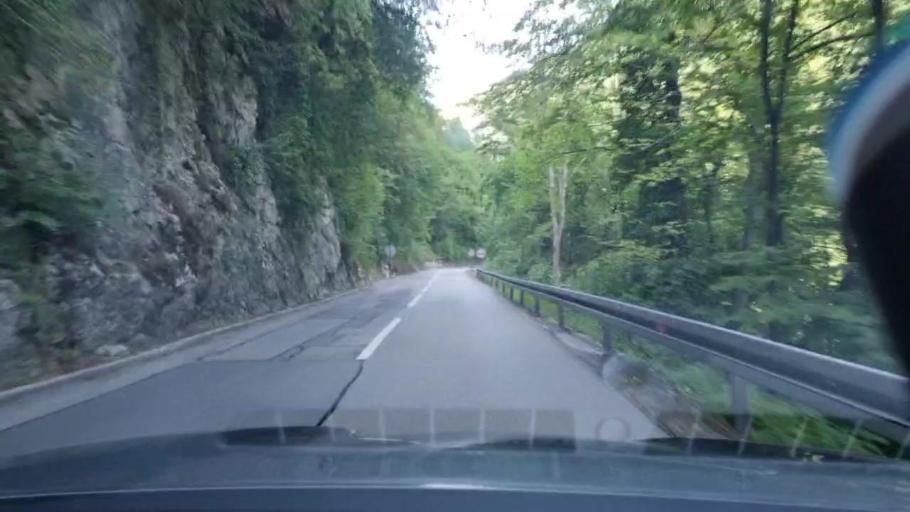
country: BA
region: Federation of Bosnia and Herzegovina
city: Stijena
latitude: 44.8783
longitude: 16.0712
